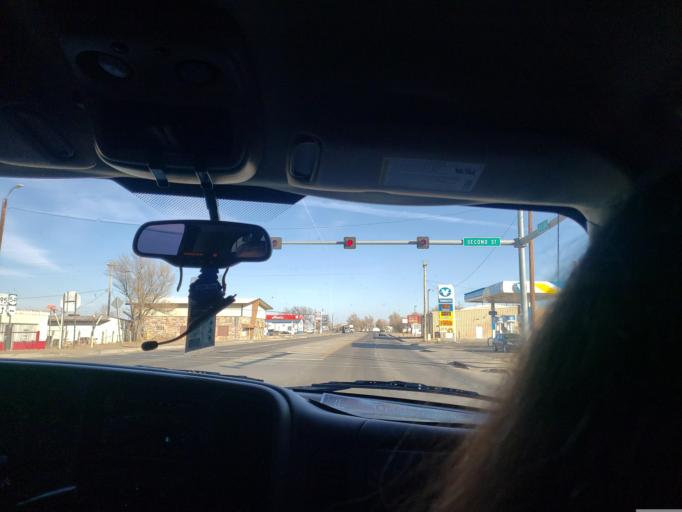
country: US
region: Oklahoma
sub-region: Texas County
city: Goodwell
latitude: 36.5018
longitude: -101.7835
